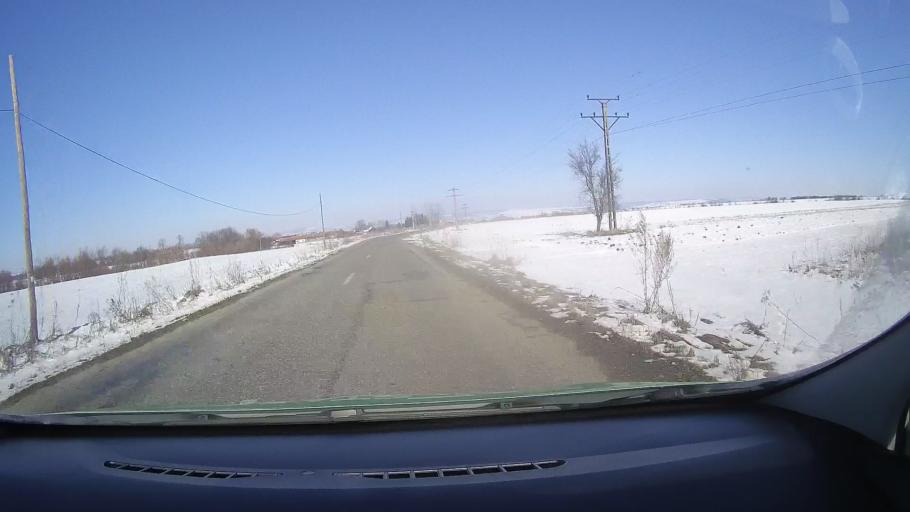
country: RO
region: Brasov
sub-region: Comuna Harseni
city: Harseni
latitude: 45.7774
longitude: 25.0010
